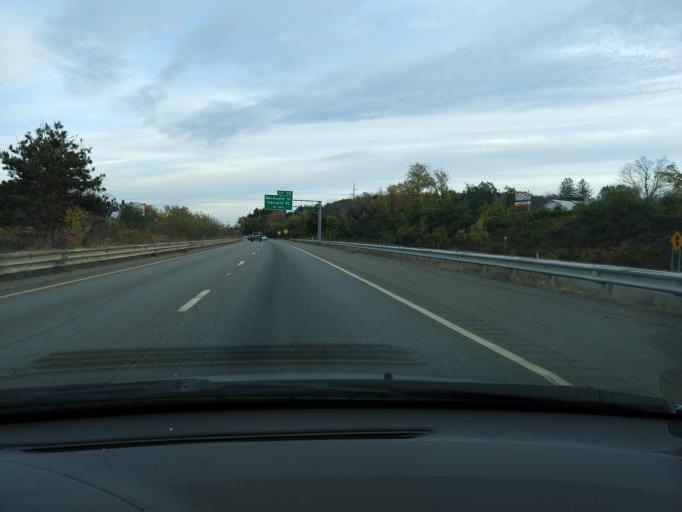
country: US
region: Massachusetts
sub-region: Worcester County
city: Leominster
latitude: 42.5221
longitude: -71.7204
